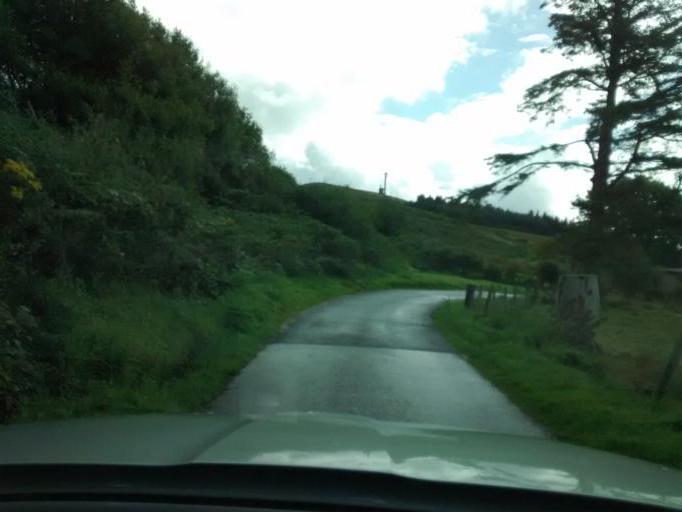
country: GB
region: Scotland
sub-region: North Ayrshire
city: Isle of Arran
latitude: 55.5746
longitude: -5.3453
